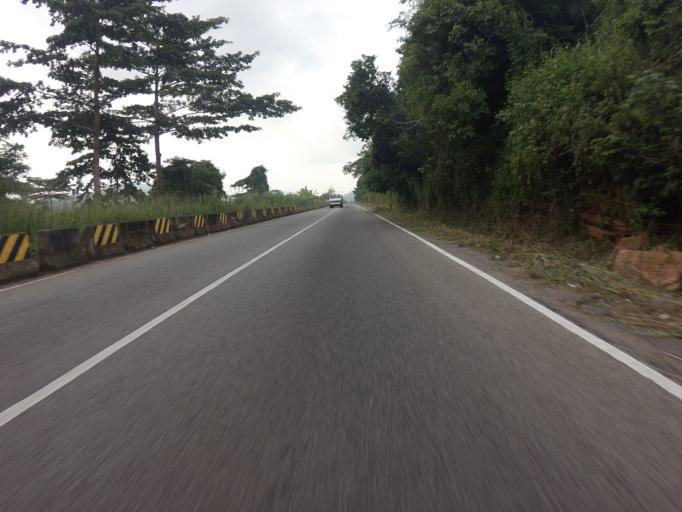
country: GH
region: Volta
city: Ho
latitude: 6.6328
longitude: 0.4642
